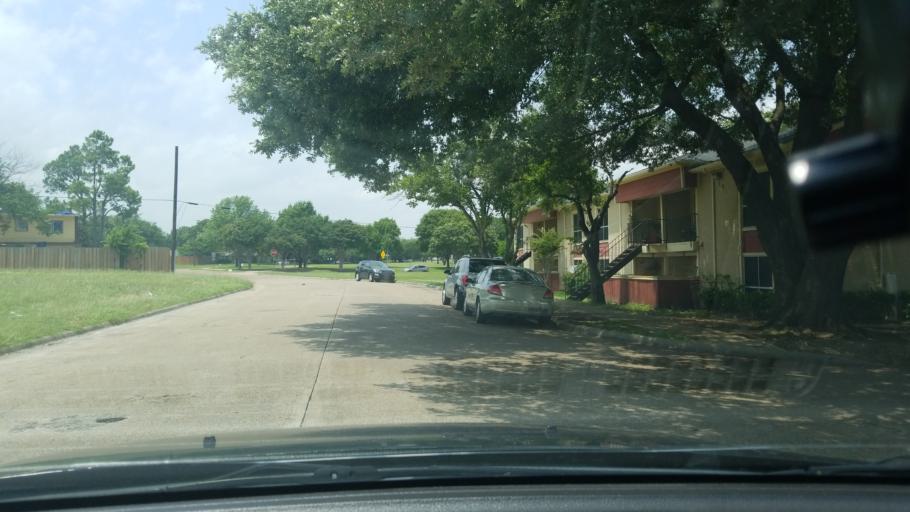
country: US
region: Texas
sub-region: Dallas County
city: Mesquite
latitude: 32.7945
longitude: -96.6444
